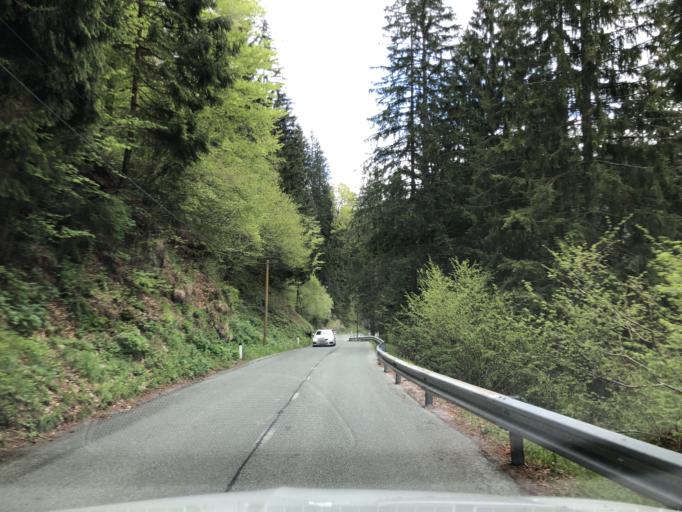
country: SI
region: Kranjska Gora
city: Kranjska Gora
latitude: 46.5021
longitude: 13.7551
